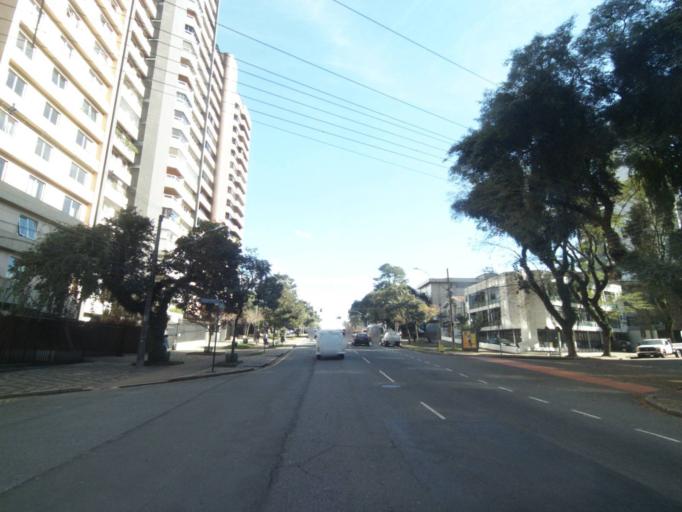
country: BR
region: Parana
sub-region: Curitiba
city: Curitiba
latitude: -25.4471
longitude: -49.2912
